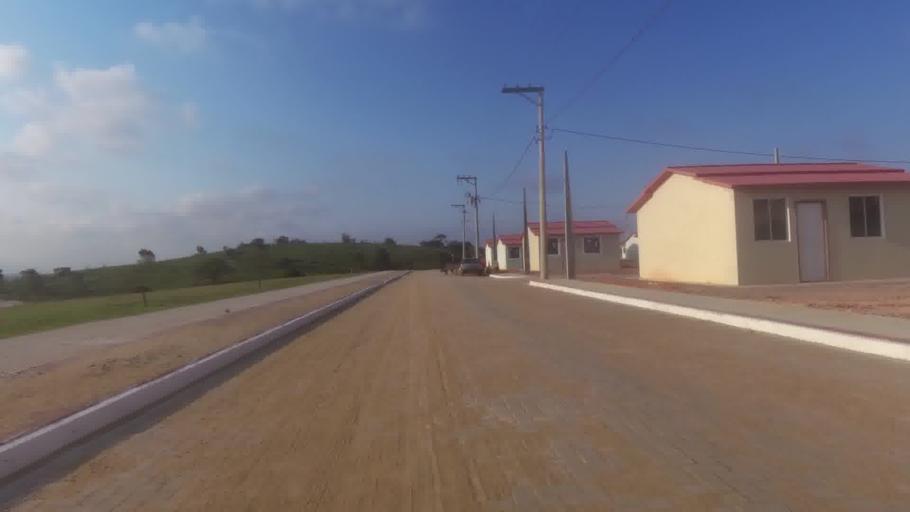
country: BR
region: Espirito Santo
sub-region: Itapemirim
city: Itapemirim
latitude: -21.0165
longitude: -40.8352
